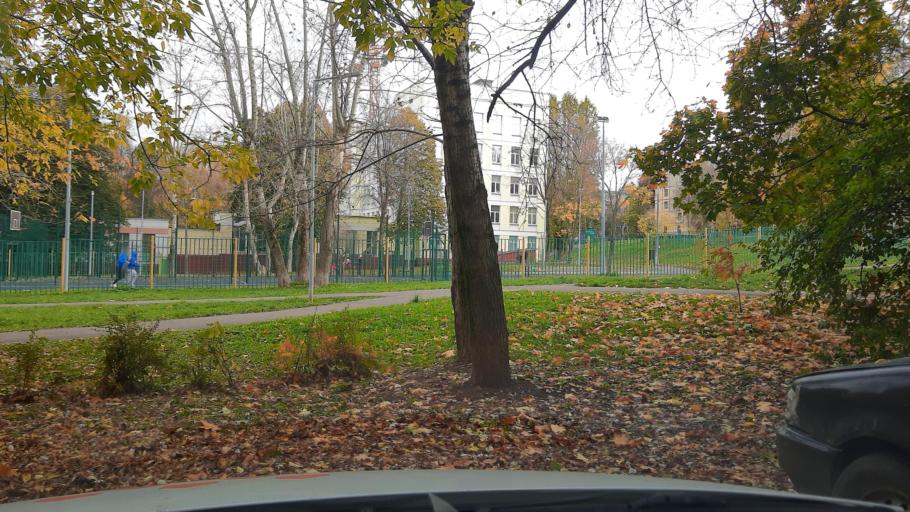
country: RU
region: Moscow
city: Zyuzino
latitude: 55.6525
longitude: 37.5750
